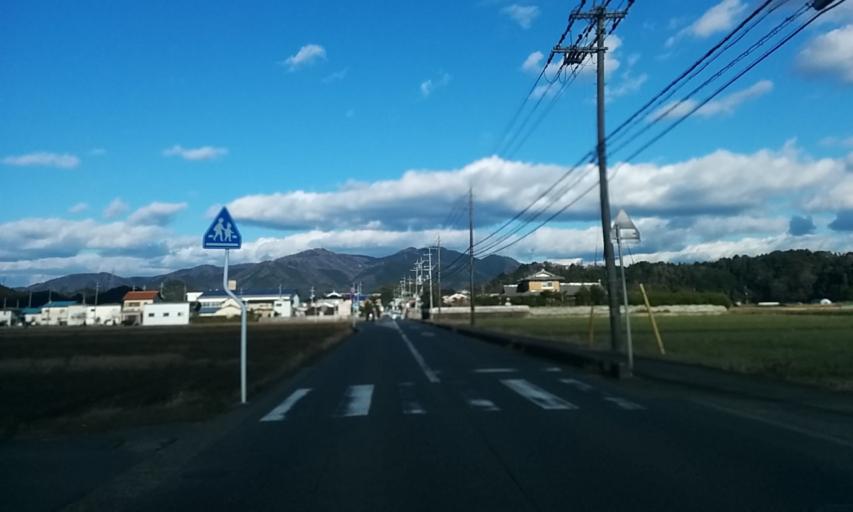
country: JP
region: Kyoto
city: Fukuchiyama
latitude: 35.2999
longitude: 135.0948
